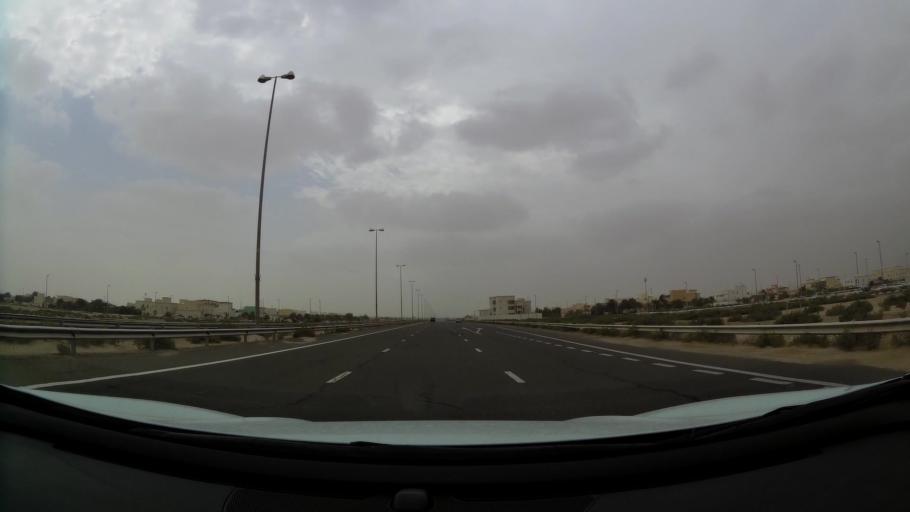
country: AE
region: Abu Dhabi
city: Abu Dhabi
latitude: 24.3735
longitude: 54.6644
